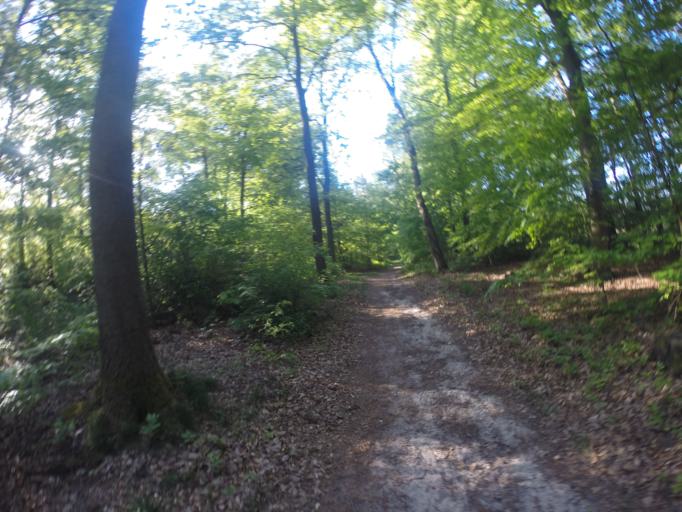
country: NL
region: Gelderland
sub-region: Gemeente Montferland
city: s-Heerenberg
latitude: 51.8872
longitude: 6.2364
